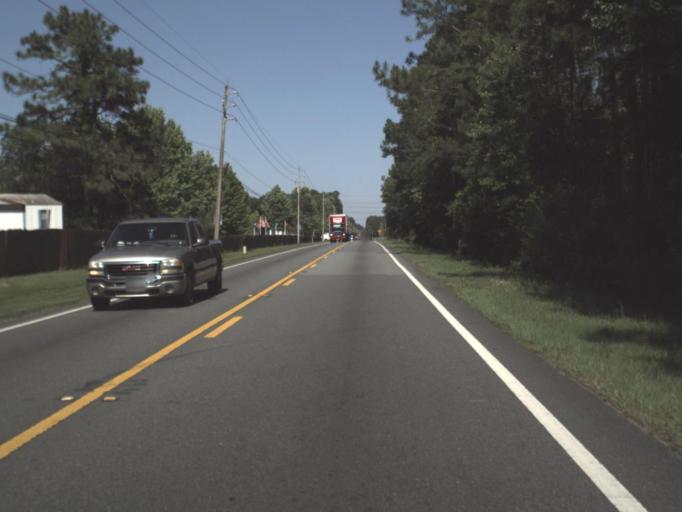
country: US
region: Florida
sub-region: Duval County
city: Baldwin
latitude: 30.3167
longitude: -81.8269
